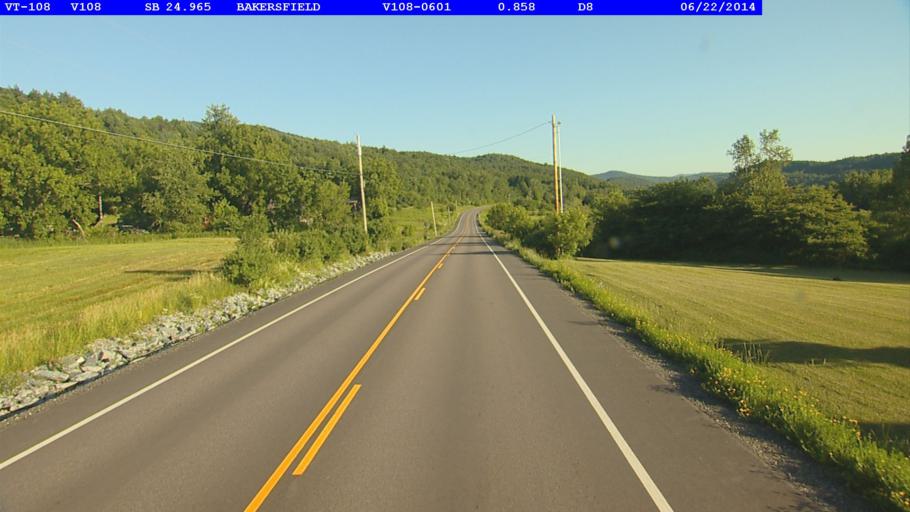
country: US
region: Vermont
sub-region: Franklin County
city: Enosburg Falls
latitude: 44.7455
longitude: -72.8234
